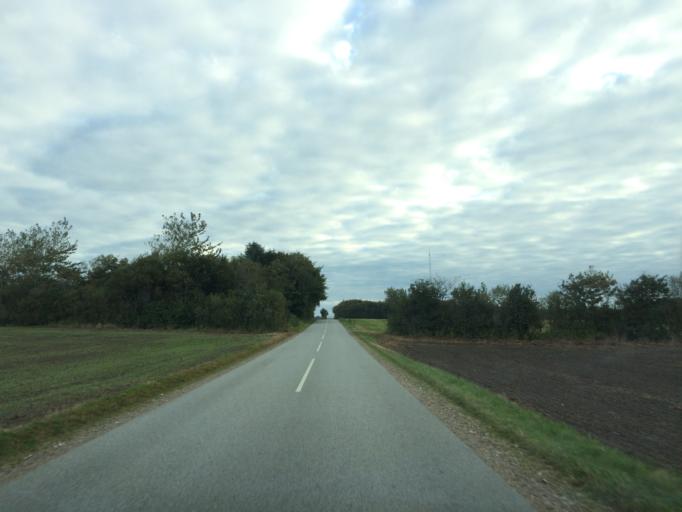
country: DK
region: Central Jutland
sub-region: Ringkobing-Skjern Kommune
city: Skjern
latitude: 56.0532
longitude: 8.4574
